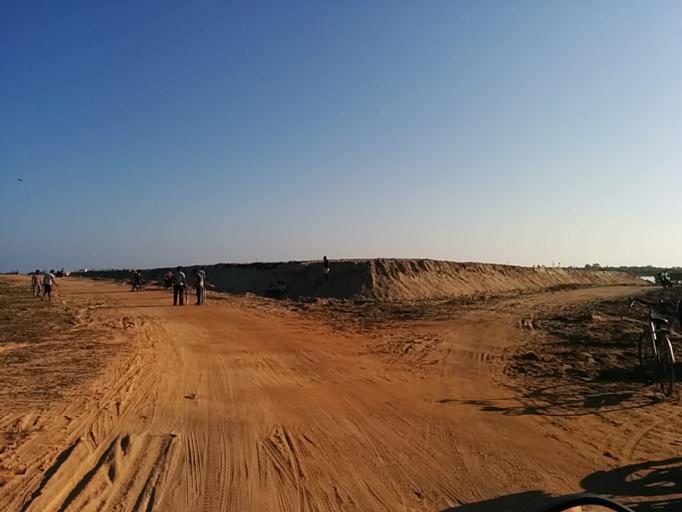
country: IN
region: Pondicherry
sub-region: Puducherry
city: Puducherry
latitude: 11.9102
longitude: 79.8286
